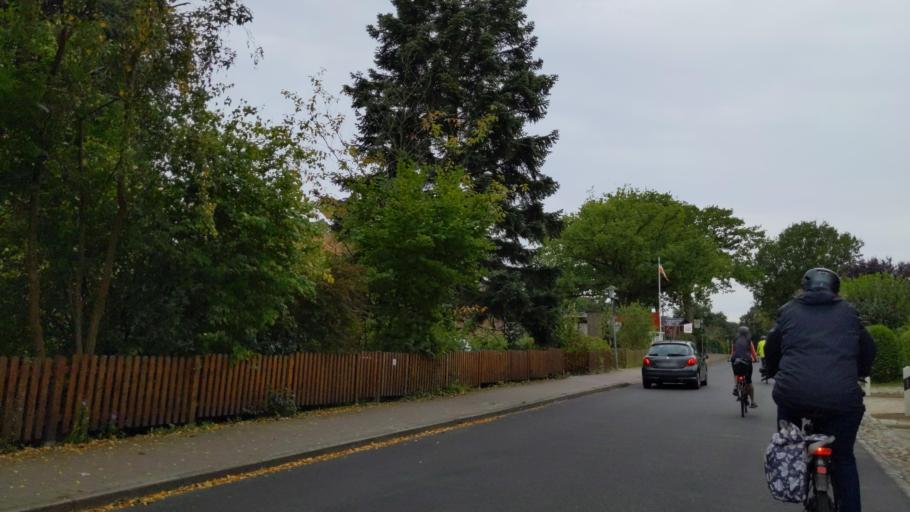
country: DE
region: Schleswig-Holstein
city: Bak
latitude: 53.7136
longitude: 10.7820
